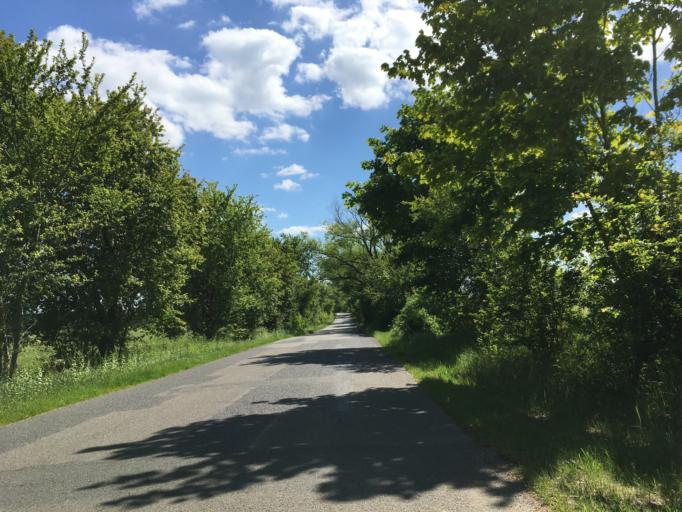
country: DE
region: Brandenburg
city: Rudnitz
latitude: 52.7067
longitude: 13.6616
